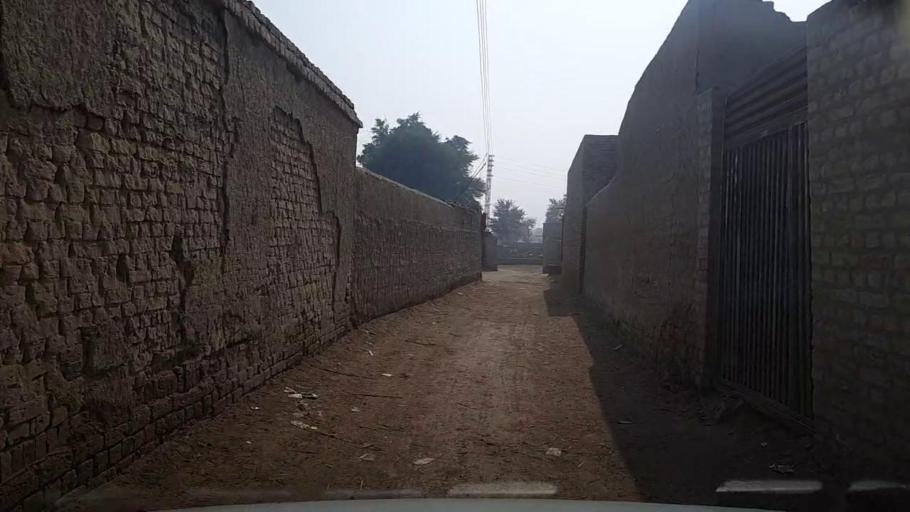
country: PK
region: Sindh
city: Setharja Old
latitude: 27.1531
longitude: 68.4642
